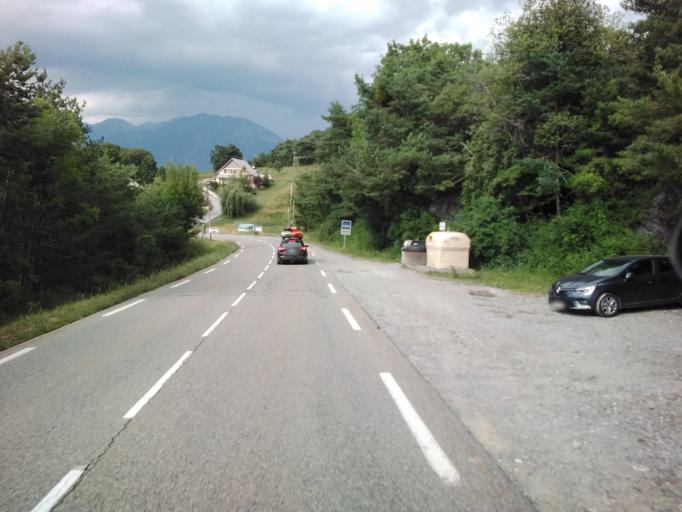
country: FR
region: Provence-Alpes-Cote d'Azur
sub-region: Departement des Hautes-Alpes
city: Chorges
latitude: 44.5099
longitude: 6.3560
